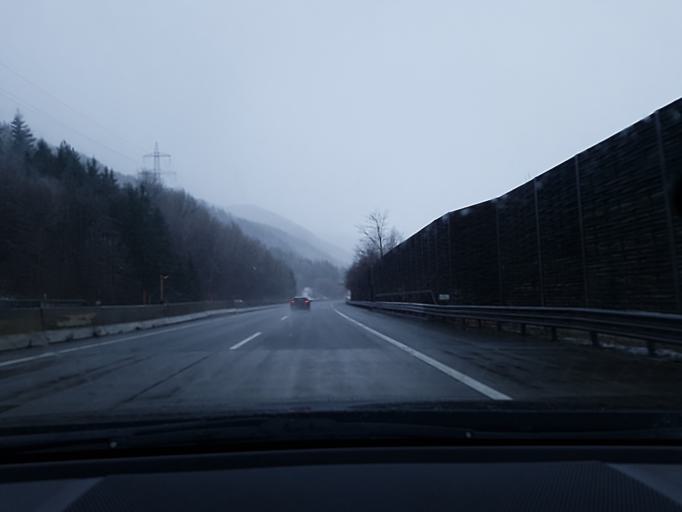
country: AT
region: Salzburg
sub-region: Politischer Bezirk Hallein
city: Kuchl
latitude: 47.6248
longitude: 13.1353
